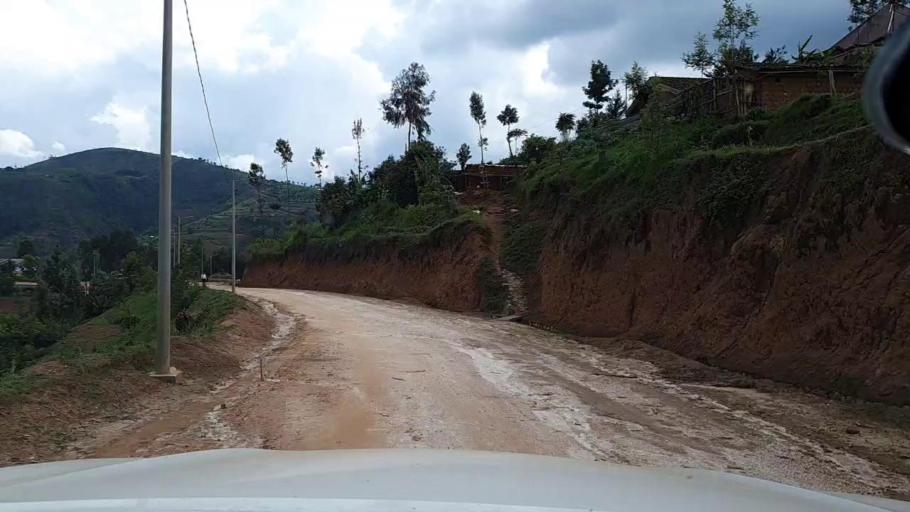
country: RW
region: Southern Province
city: Nzega
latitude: -2.6926
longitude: 29.4432
